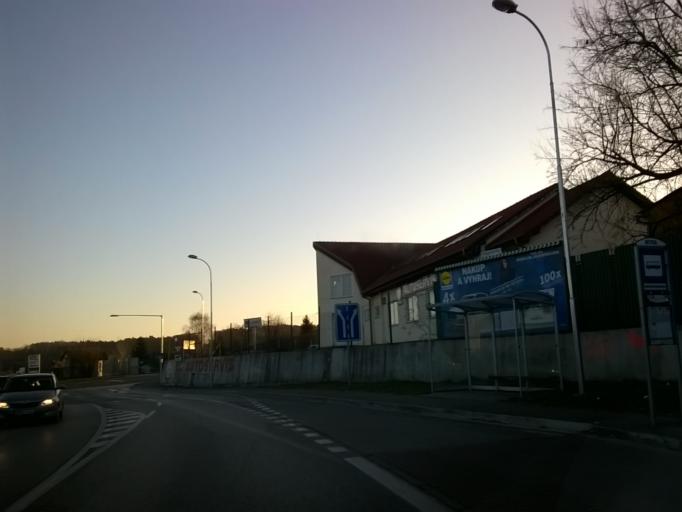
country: SK
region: Nitriansky
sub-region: Okres Nitra
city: Nitra
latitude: 48.2880
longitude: 18.0727
